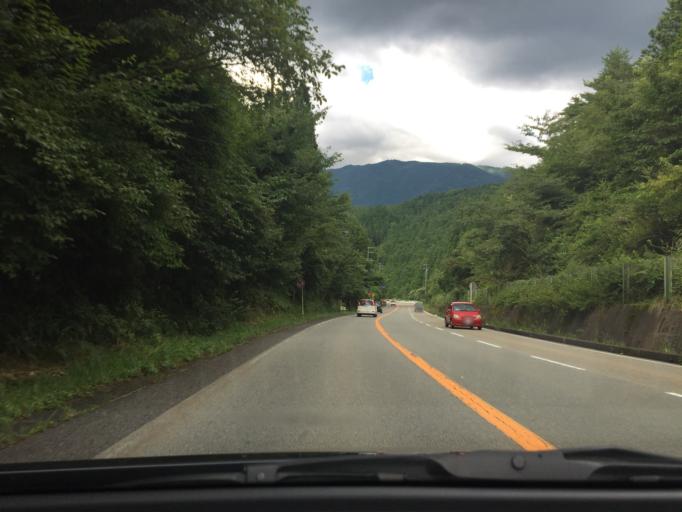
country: JP
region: Gifu
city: Nakatsugawa
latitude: 35.7532
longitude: 137.3276
